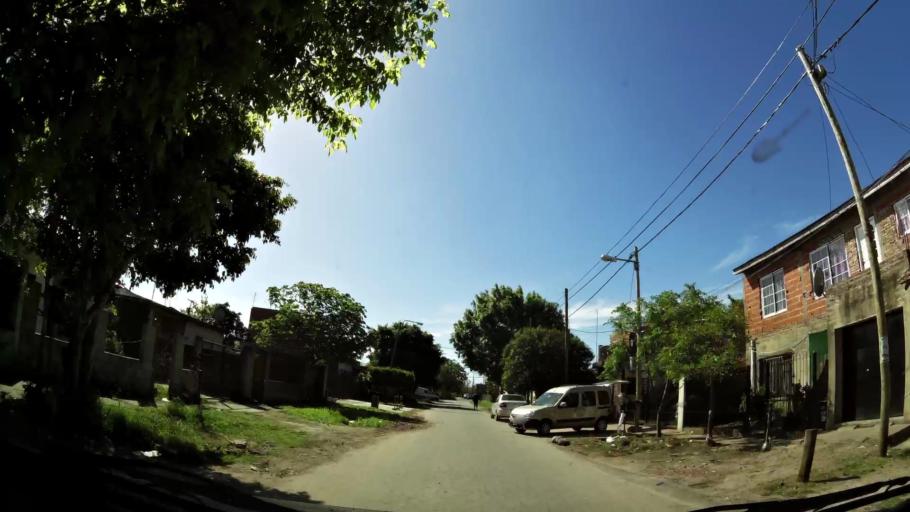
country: AR
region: Buenos Aires
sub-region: Partido de Quilmes
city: Quilmes
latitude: -34.7974
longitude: -58.2488
